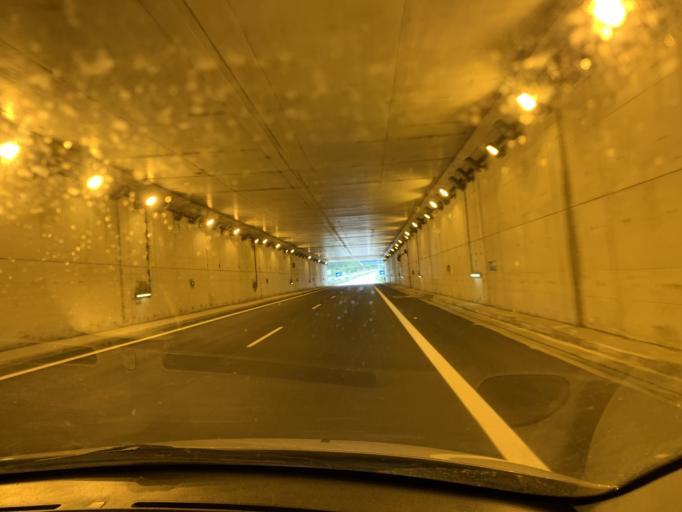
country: ES
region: Asturias
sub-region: Province of Asturias
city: Tapia de Casariego
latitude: 43.5422
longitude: -6.9636
